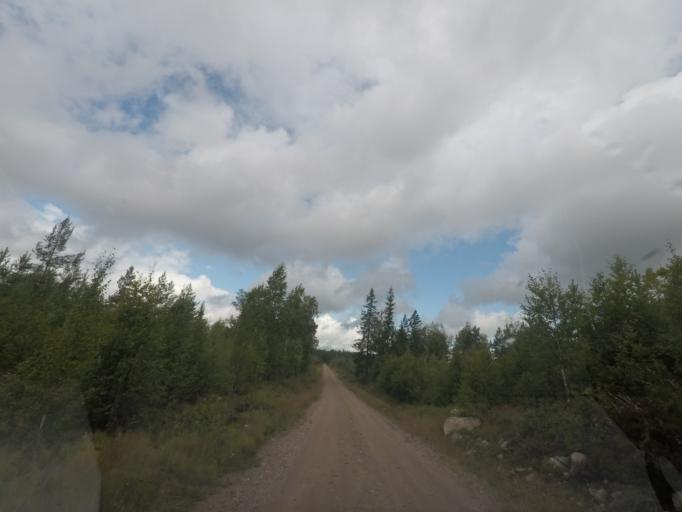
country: SE
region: Vaermland
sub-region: Filipstads Kommun
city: Lesjofors
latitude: 60.0726
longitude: 14.4299
